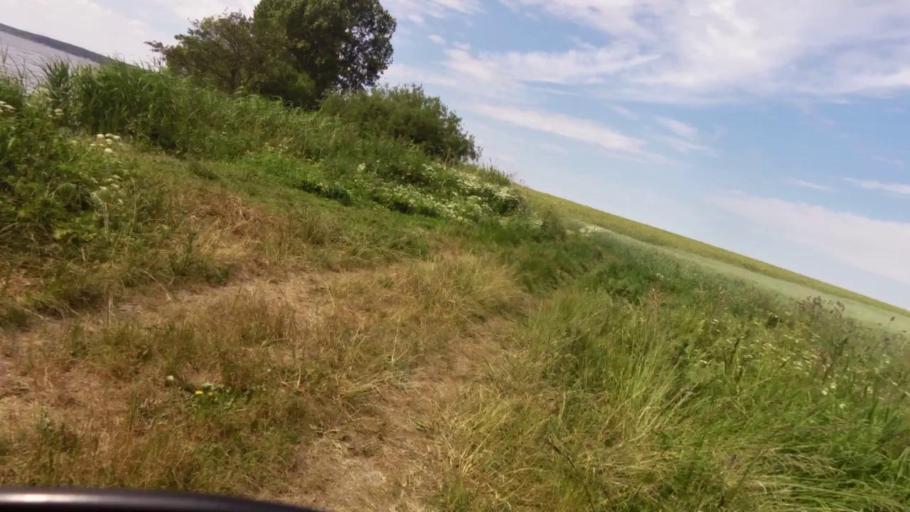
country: PL
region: West Pomeranian Voivodeship
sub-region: Powiat kamienski
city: Wolin
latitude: 53.8407
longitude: 14.5828
